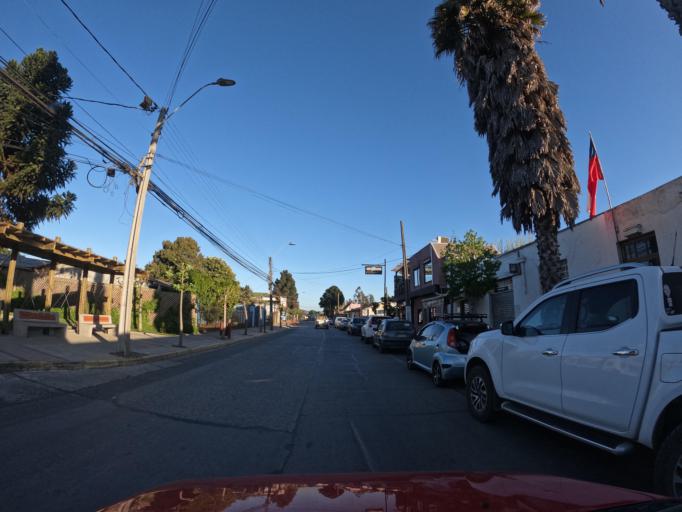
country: CL
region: Maule
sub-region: Provincia de Talca
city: Constitucion
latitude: -34.9856
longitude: -71.9875
